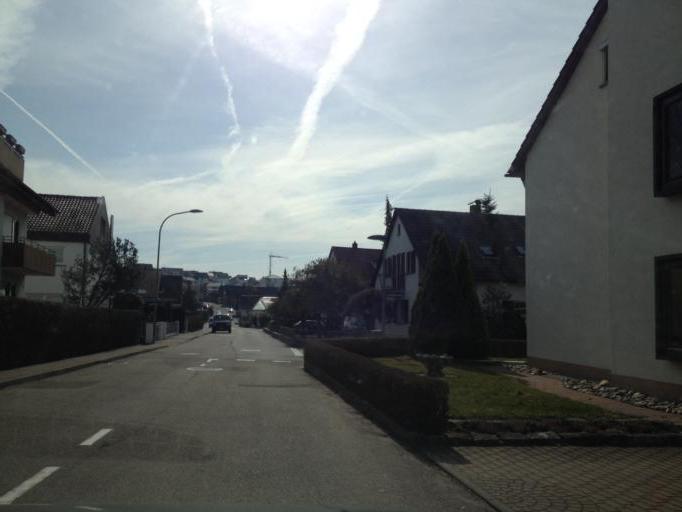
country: DE
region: Baden-Wuerttemberg
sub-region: Regierungsbezirk Stuttgart
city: Oedheim
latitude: 49.2434
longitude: 9.2629
